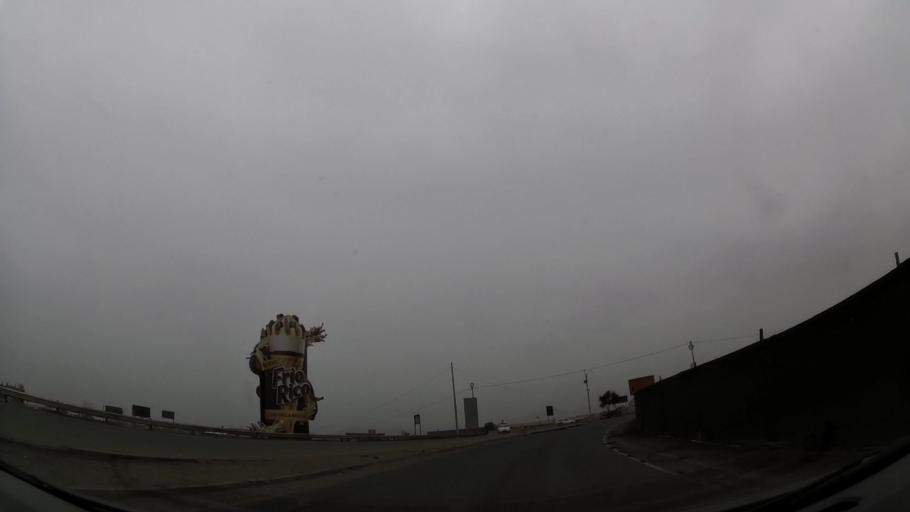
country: PE
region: Lima
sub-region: Lima
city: Punta Hermosa
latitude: -12.3030
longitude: -76.8454
